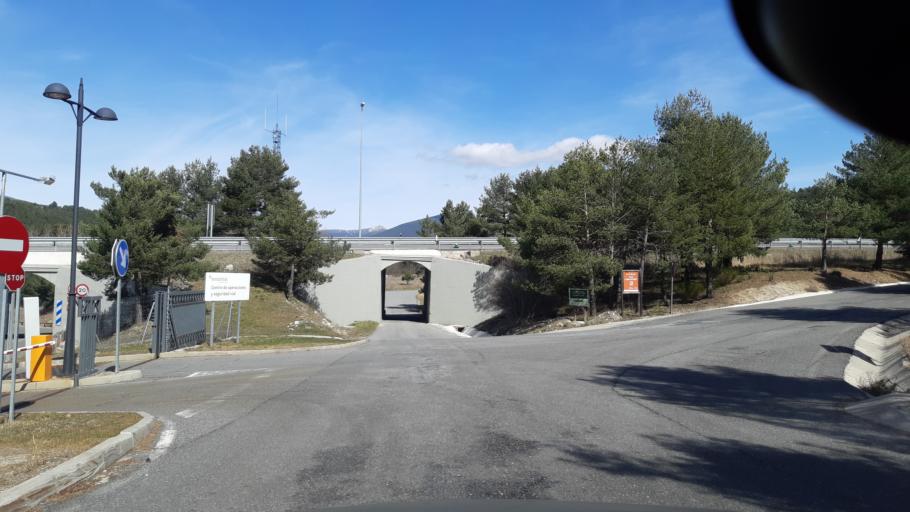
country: ES
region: Madrid
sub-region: Provincia de Madrid
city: Guadarrama
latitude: 40.7153
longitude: -4.1606
